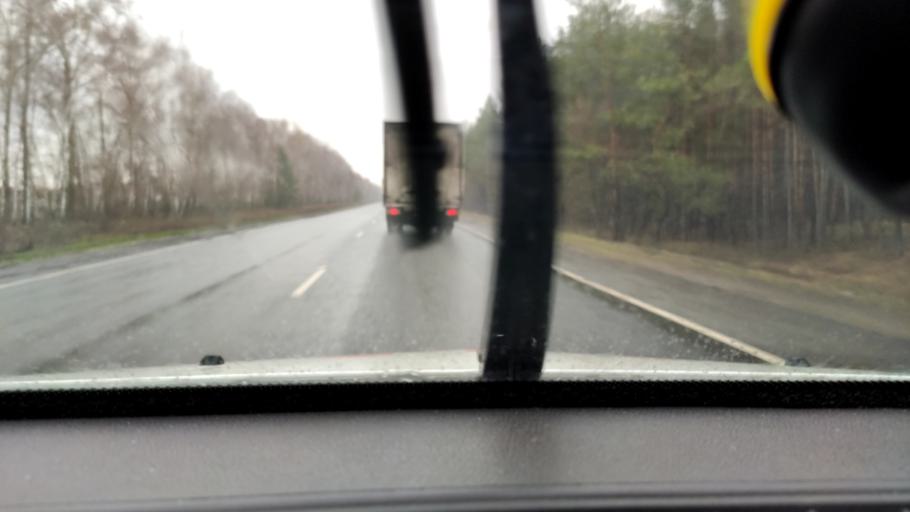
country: RU
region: Samara
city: Povolzhskiy
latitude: 53.6131
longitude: 49.6230
